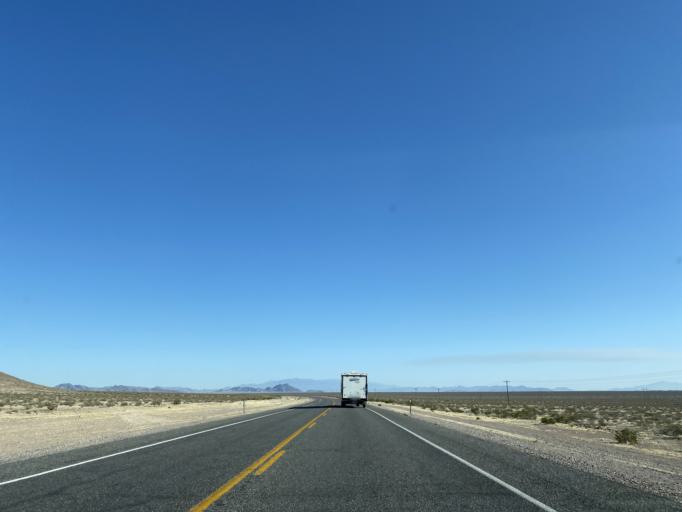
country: US
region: Nevada
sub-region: Nye County
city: Beatty
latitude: 36.6790
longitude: -116.5395
